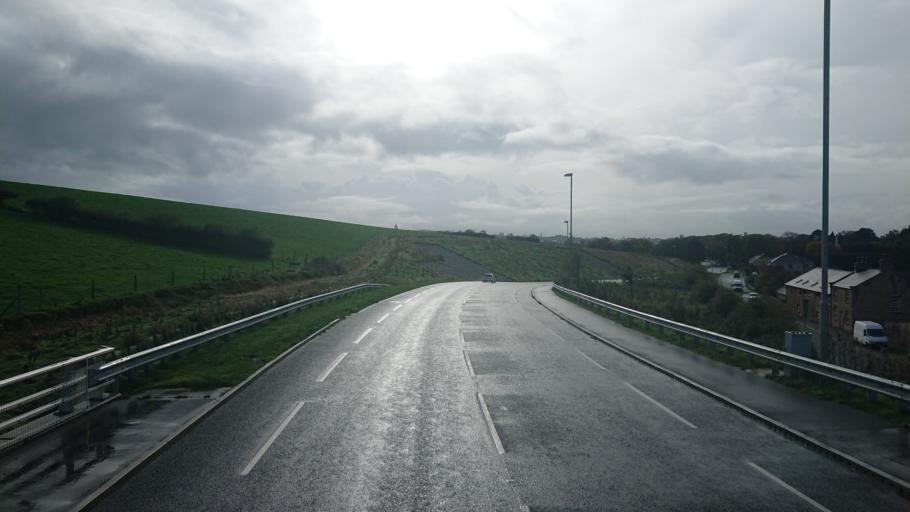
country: GB
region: England
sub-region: Lancashire
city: Bolton le Sands
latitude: 54.0720
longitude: -2.8010
